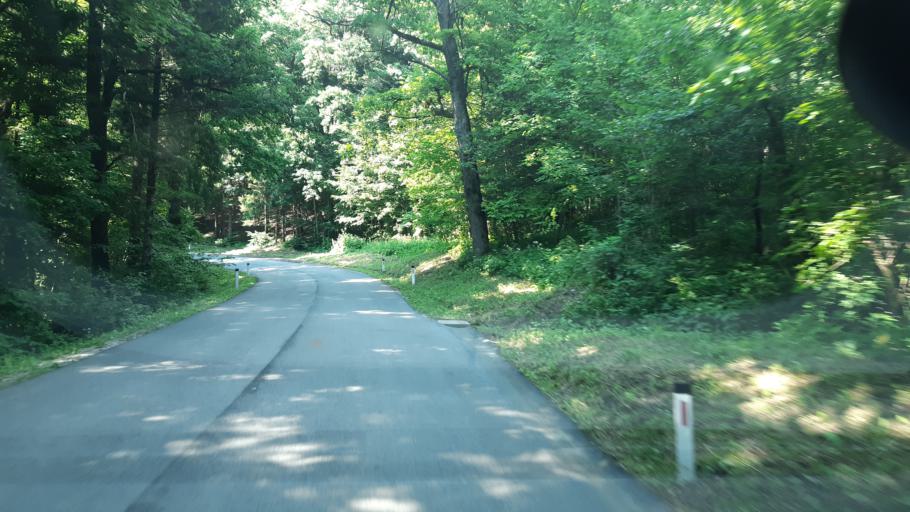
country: SI
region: Radovljica
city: Radovljica
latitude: 46.3751
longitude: 14.2165
